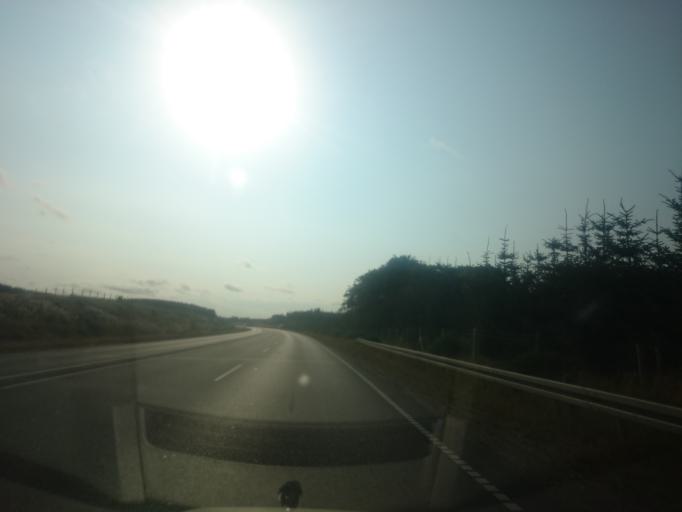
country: DK
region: South Denmark
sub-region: Vejle Kommune
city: Egtved
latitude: 55.7083
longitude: 9.2357
